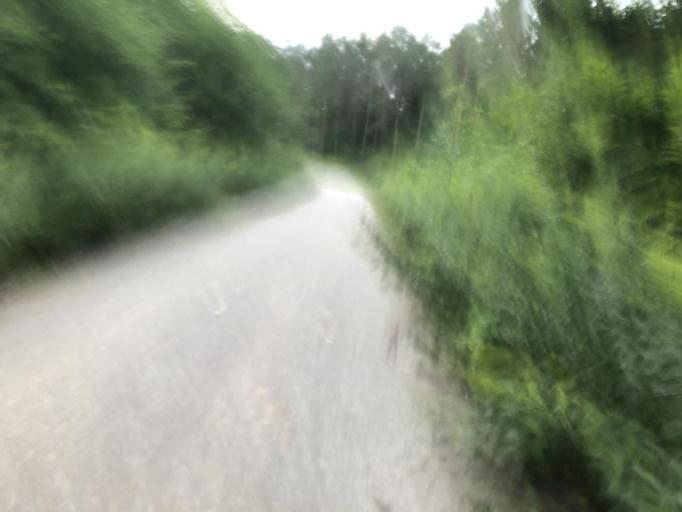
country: DE
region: Bavaria
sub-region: Regierungsbezirk Mittelfranken
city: Buckenhof
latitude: 49.5867
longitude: 11.0415
